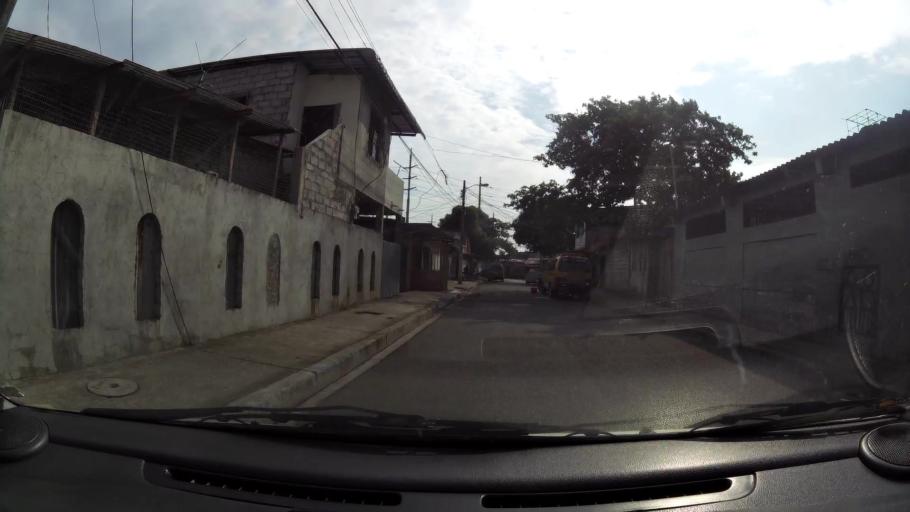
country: EC
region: Guayas
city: Guayaquil
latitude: -2.2503
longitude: -79.9084
